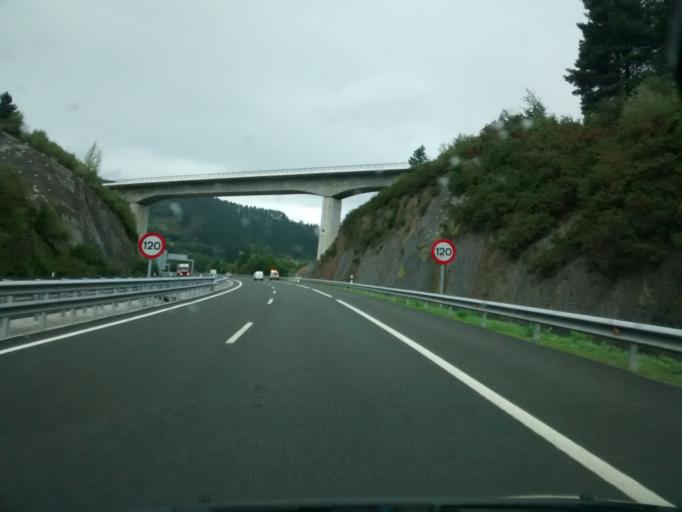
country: ES
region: Basque Country
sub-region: Provincia de Guipuzcoa
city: Bergara
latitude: 43.0971
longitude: -2.4336
